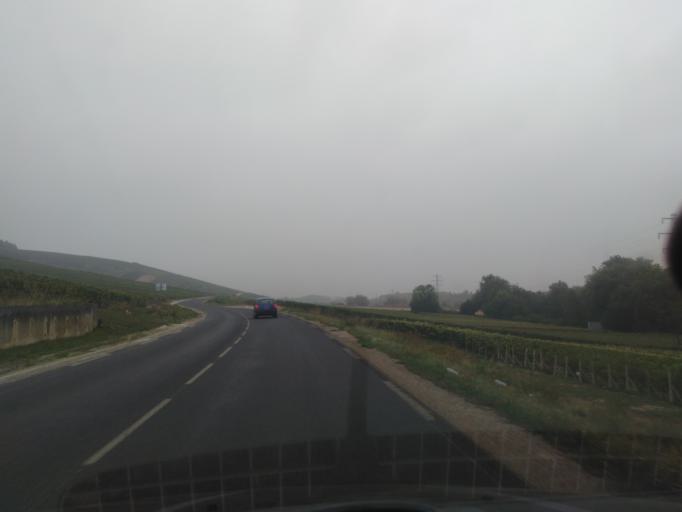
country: FR
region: Champagne-Ardenne
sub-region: Departement de la Marne
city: Damery
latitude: 49.0698
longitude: 3.8953
